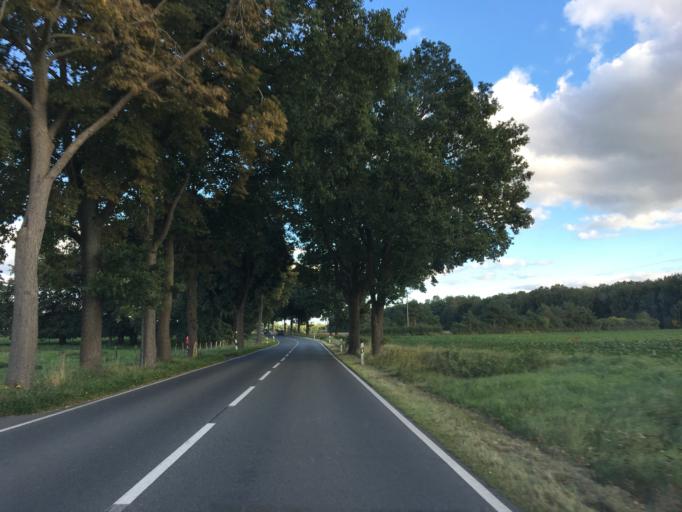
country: DE
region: Lower Saxony
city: Westergellersen
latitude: 53.2311
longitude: 10.2643
